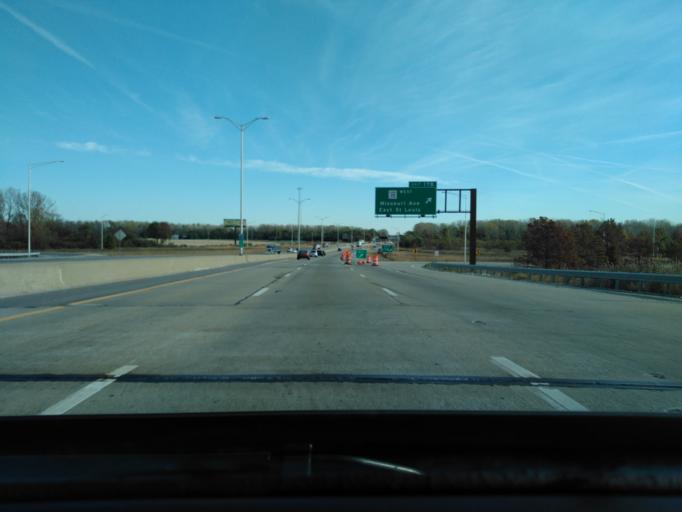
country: US
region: Illinois
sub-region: Saint Clair County
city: Alorton
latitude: 38.5826
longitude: -90.1075
